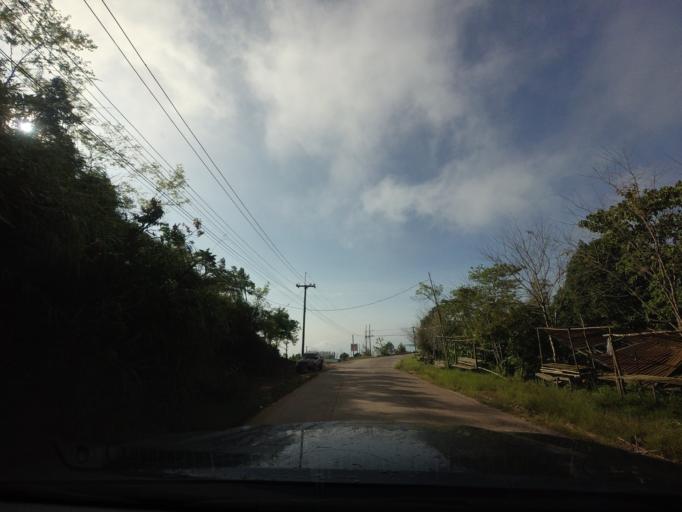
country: TH
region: Phetchabun
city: Lom Kao
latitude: 16.8950
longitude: 101.1044
